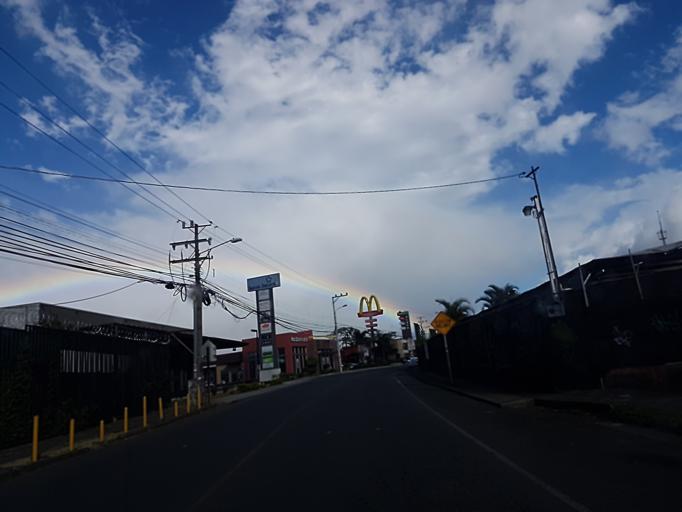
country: CR
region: San Jose
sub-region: Canton de Goicoechea
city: Guadalupe
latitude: 9.9396
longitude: -84.0568
